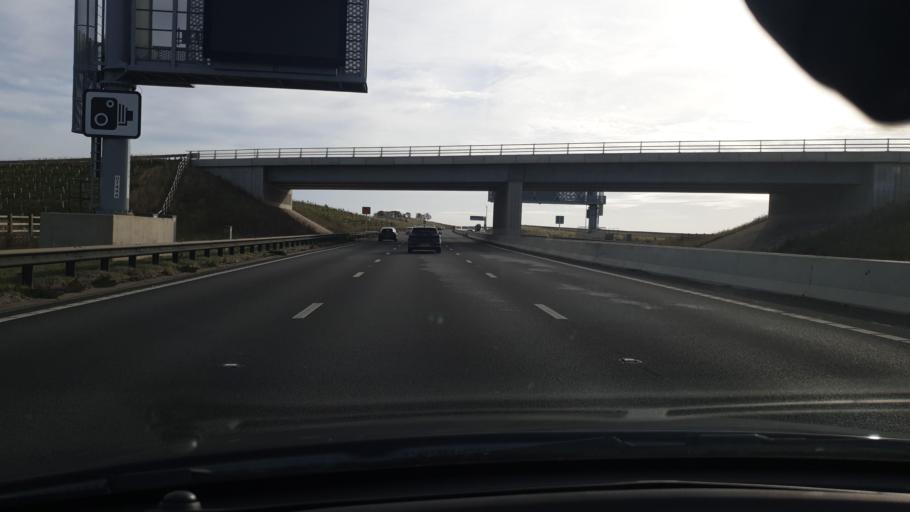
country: GB
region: England
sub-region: Cambridgeshire
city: Brampton
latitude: 52.3002
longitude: -0.2033
